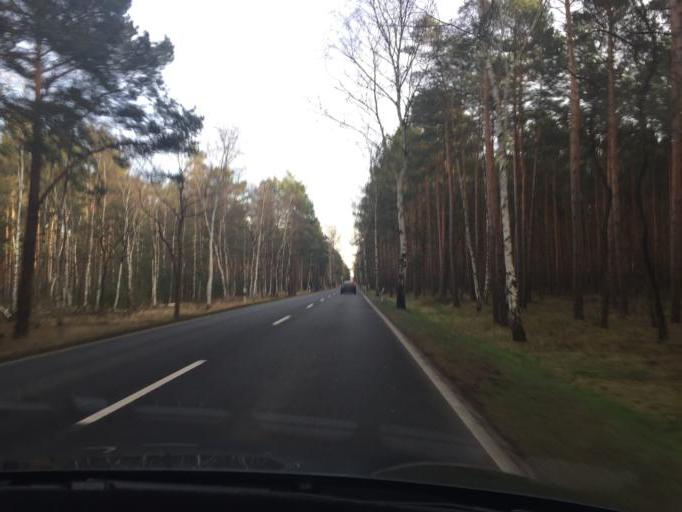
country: DE
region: Brandenburg
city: Heinersbruck
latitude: 51.7297
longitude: 14.4410
